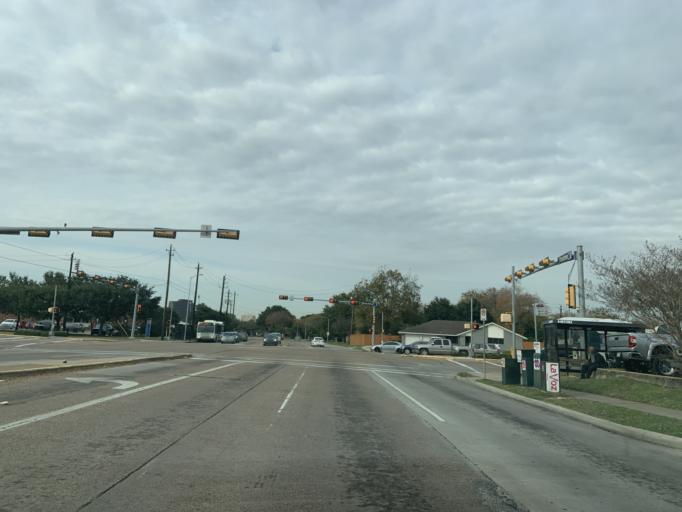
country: US
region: Texas
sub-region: Harris County
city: Bellaire
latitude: 29.6916
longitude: -95.5098
